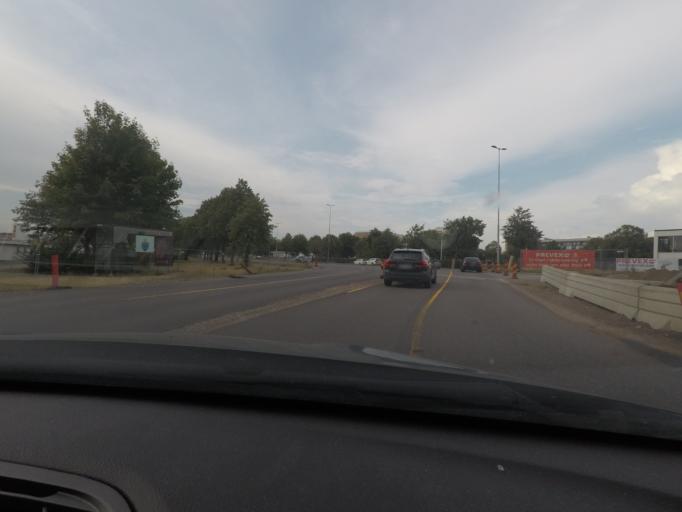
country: SE
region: Halland
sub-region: Halmstads Kommun
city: Fyllinge
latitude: 56.6568
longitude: 12.8983
